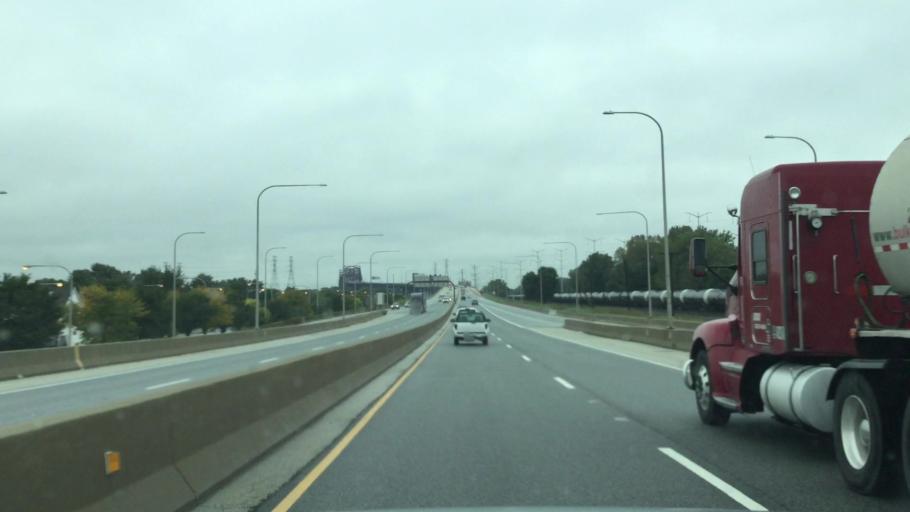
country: US
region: Indiana
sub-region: Lake County
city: Whiting
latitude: 41.7069
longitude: -87.5282
